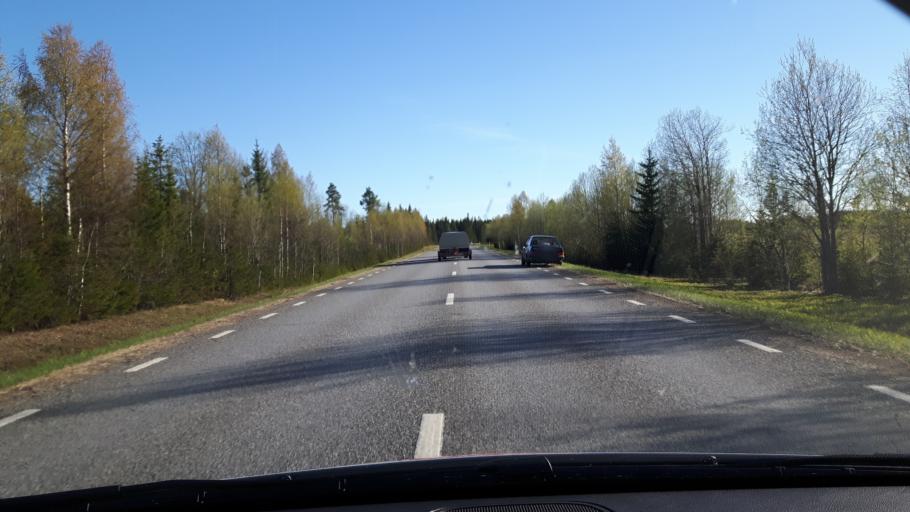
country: SE
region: Jaemtland
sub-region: Stroemsunds Kommun
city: Stroemsund
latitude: 63.5124
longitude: 15.2861
